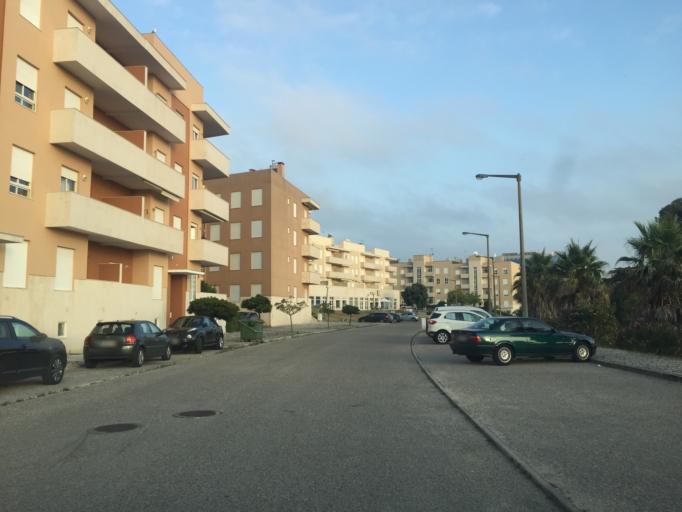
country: PT
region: Coimbra
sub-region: Figueira da Foz
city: Buarcos
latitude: 40.1597
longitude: -8.8681
